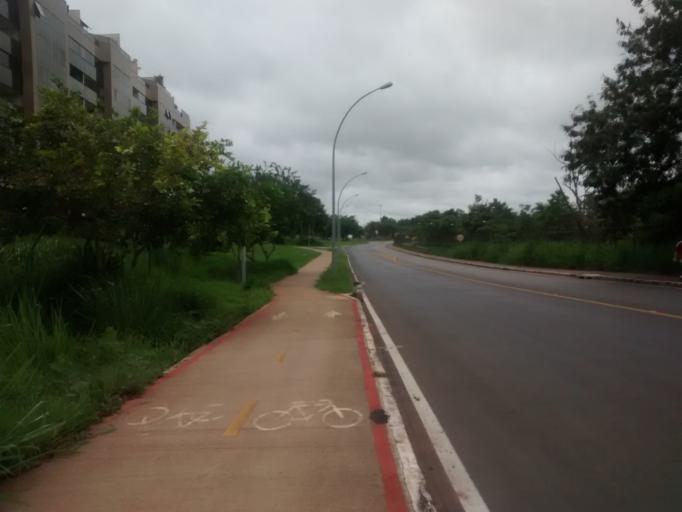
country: BR
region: Federal District
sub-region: Brasilia
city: Brasilia
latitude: -15.7470
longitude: -47.8854
